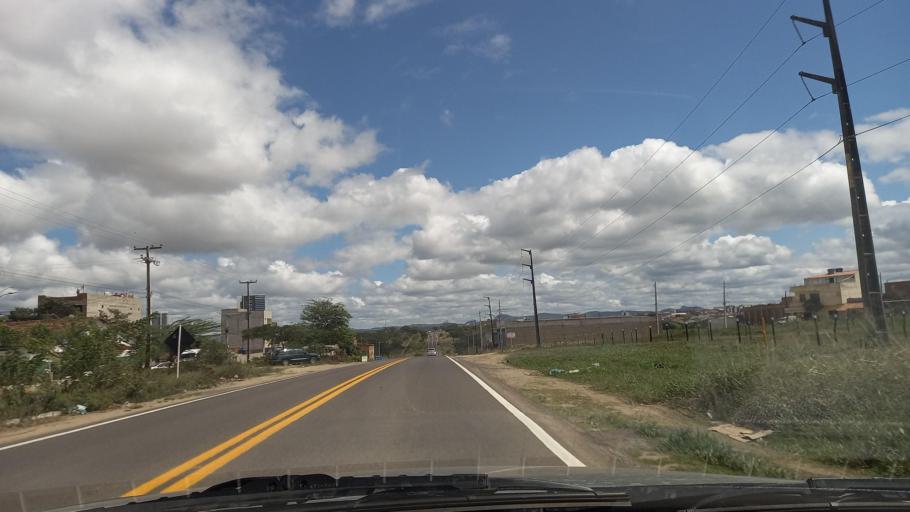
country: BR
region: Pernambuco
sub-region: Caruaru
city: Caruaru
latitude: -8.2577
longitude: -35.9555
